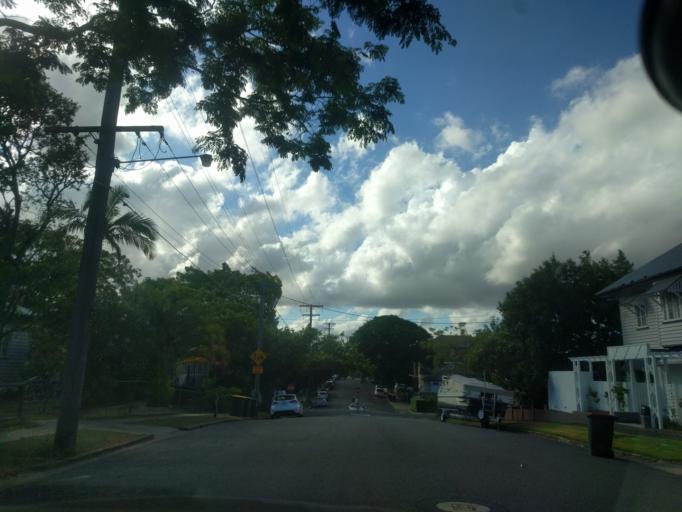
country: AU
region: Queensland
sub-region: Brisbane
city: Balmoral
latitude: -27.4716
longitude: 153.0498
